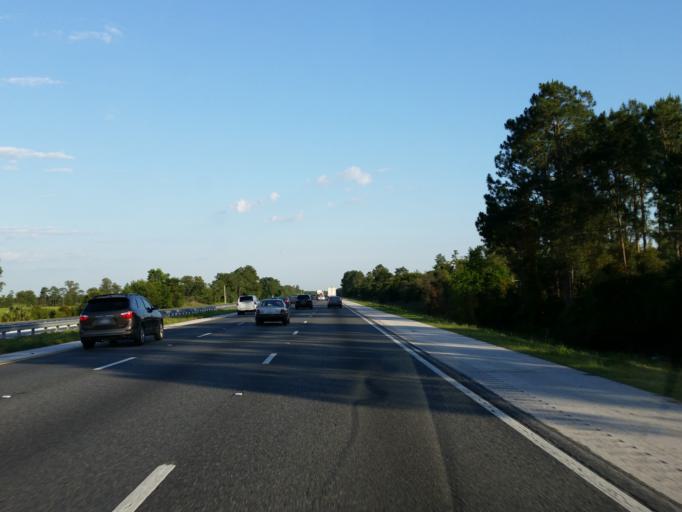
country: US
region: Florida
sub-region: Marion County
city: Ocala
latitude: 29.0742
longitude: -82.1829
